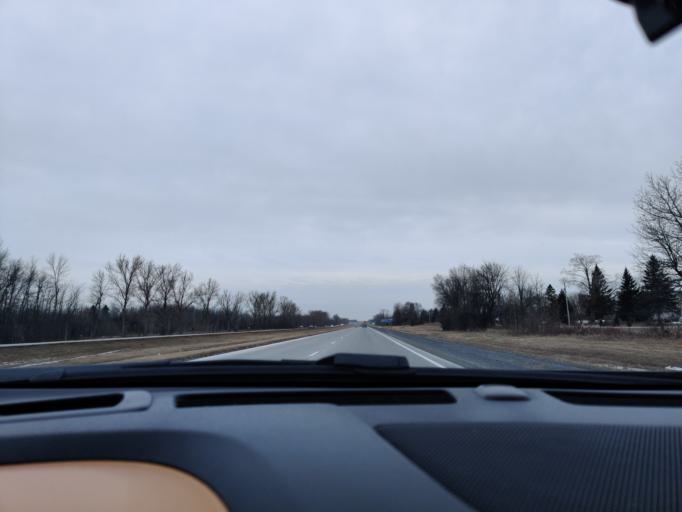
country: US
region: New York
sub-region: St. Lawrence County
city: Massena
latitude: 45.0215
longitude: -74.9723
